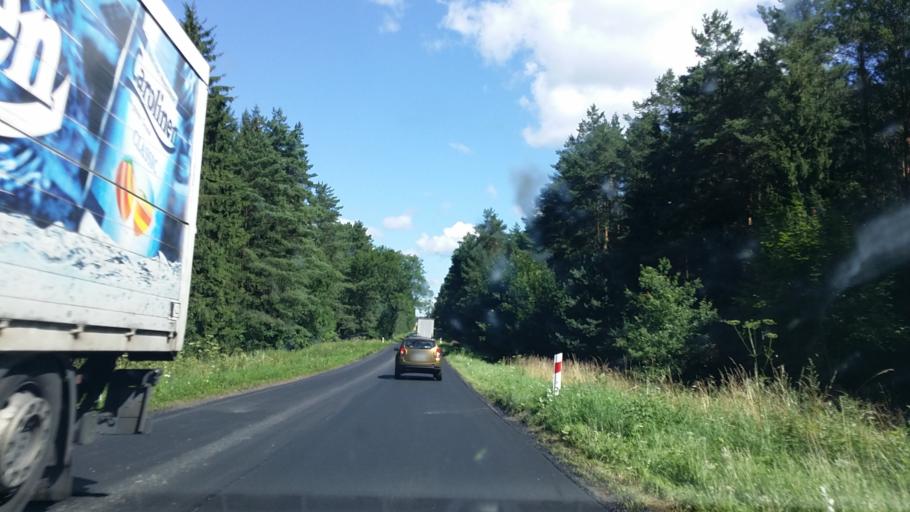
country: PL
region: West Pomeranian Voivodeship
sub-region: Powiat drawski
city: Kalisz Pomorski
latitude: 53.3512
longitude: 15.8874
